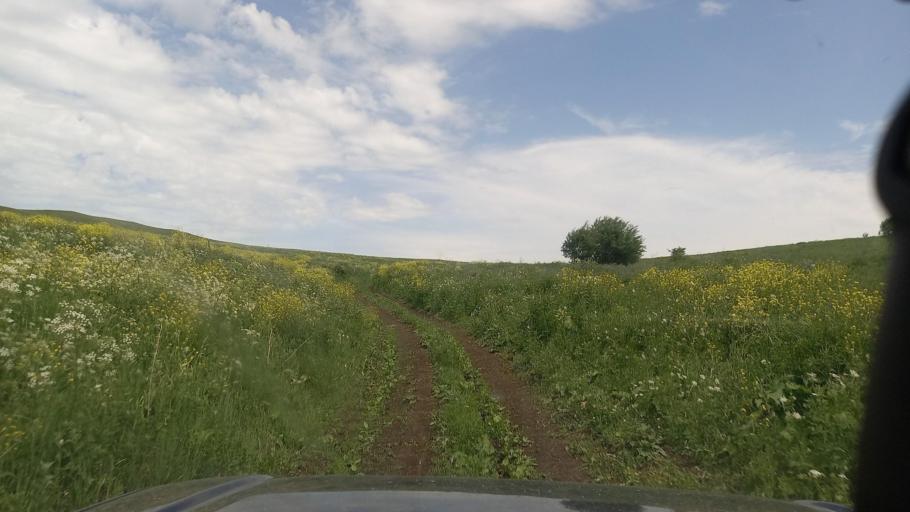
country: RU
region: Karachayevo-Cherkesiya
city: Pregradnaya
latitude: 44.0708
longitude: 41.2859
